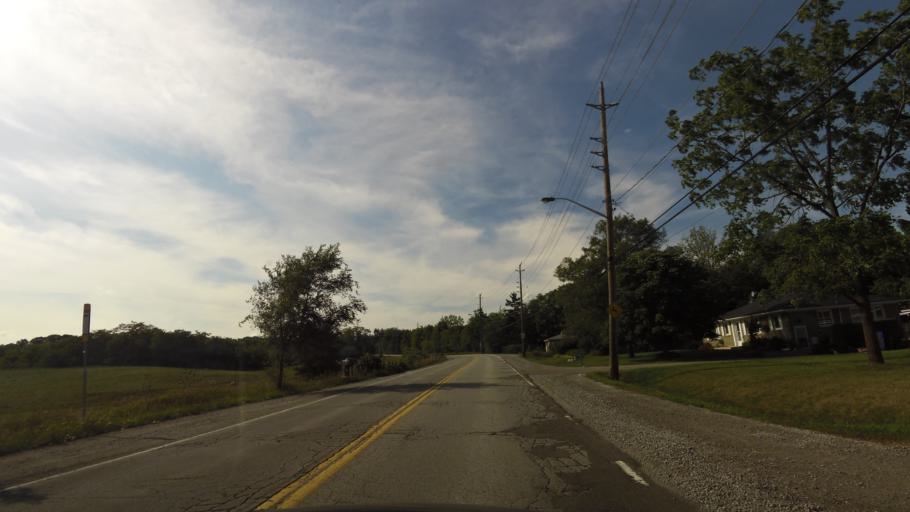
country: CA
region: Ontario
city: Hamilton
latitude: 43.3206
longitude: -79.8718
